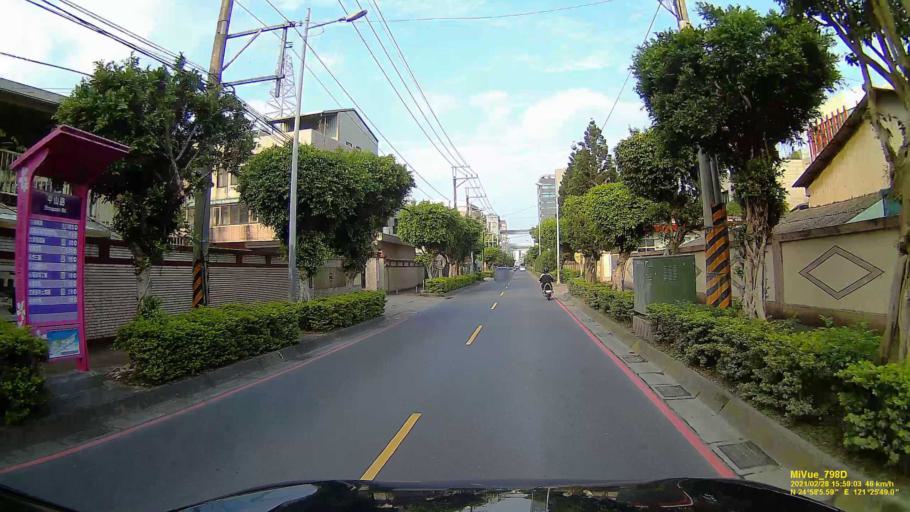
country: TW
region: Taipei
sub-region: Taipei
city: Banqiao
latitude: 24.9685
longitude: 121.4305
